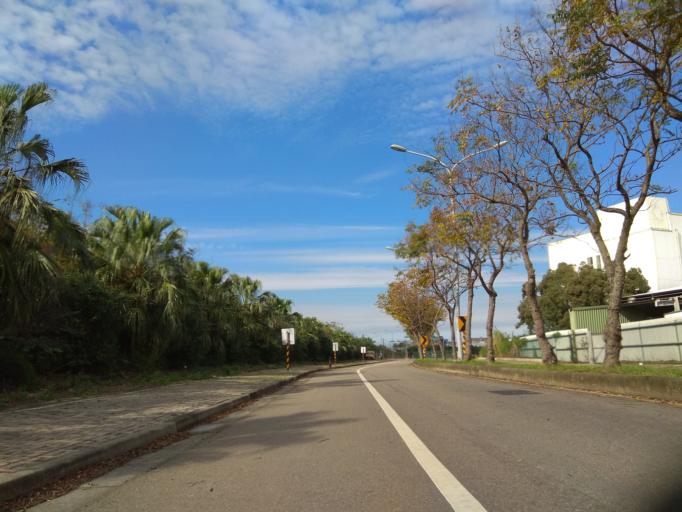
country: TW
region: Taiwan
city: Taoyuan City
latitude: 25.0571
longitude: 121.1801
